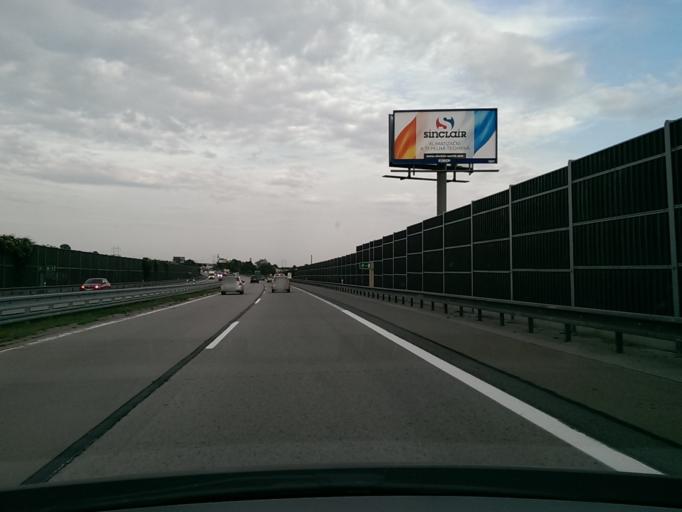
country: CZ
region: South Moravian
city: Troubsko
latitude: 49.1771
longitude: 16.4951
